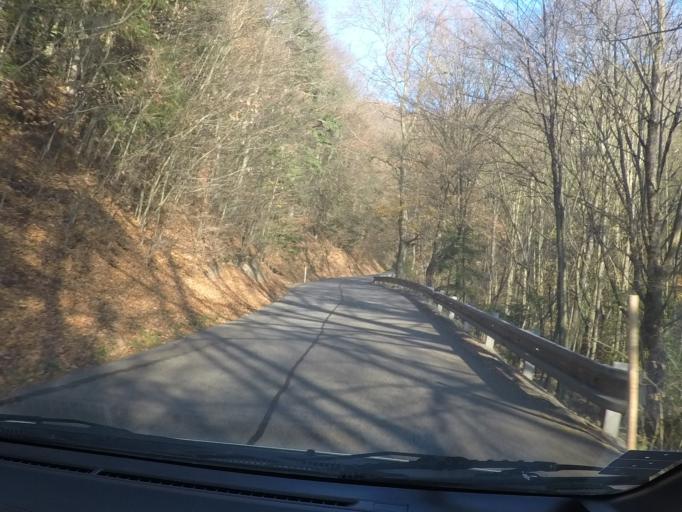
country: SK
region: Banskobystricky
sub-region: Okres Banska Bystrica
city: Banska Stiavnica
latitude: 48.4669
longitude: 18.8473
